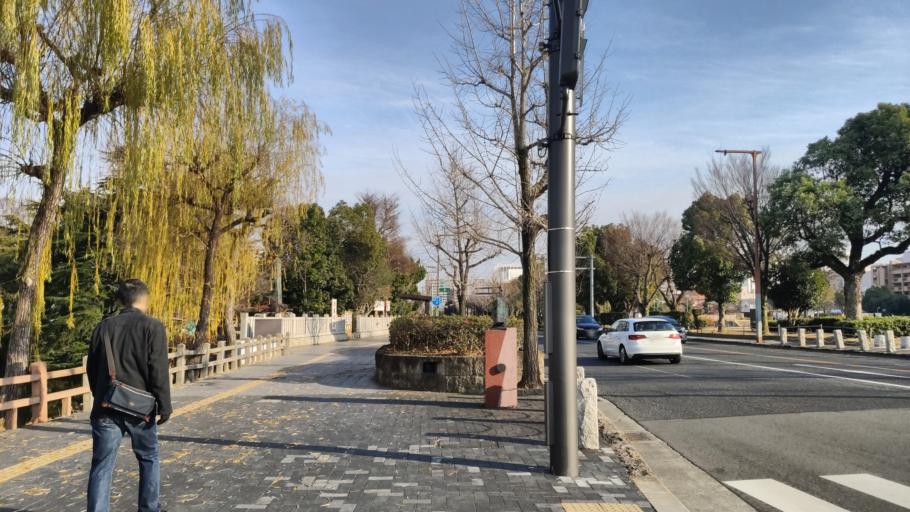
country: JP
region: Hyogo
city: Himeji
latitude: 34.8354
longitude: 134.6931
